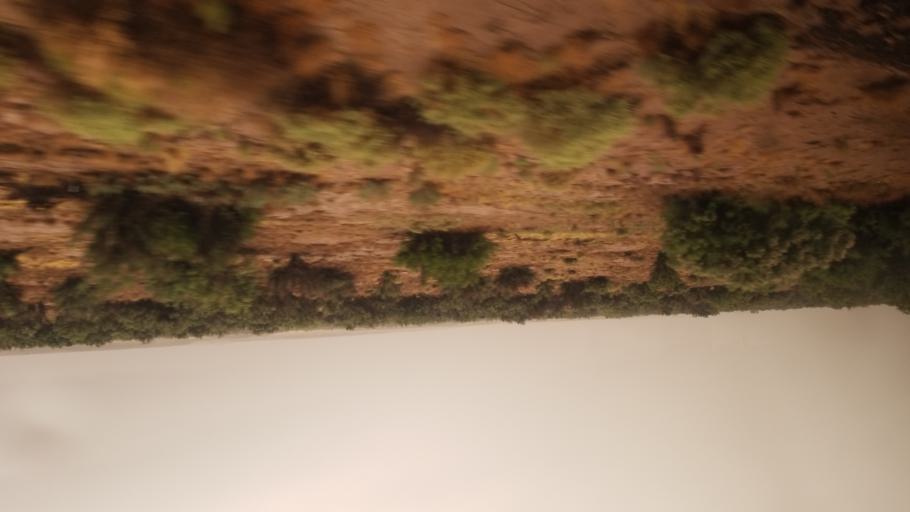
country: US
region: Arizona
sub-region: Navajo County
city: Joseph City
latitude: 34.9566
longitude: -110.3662
